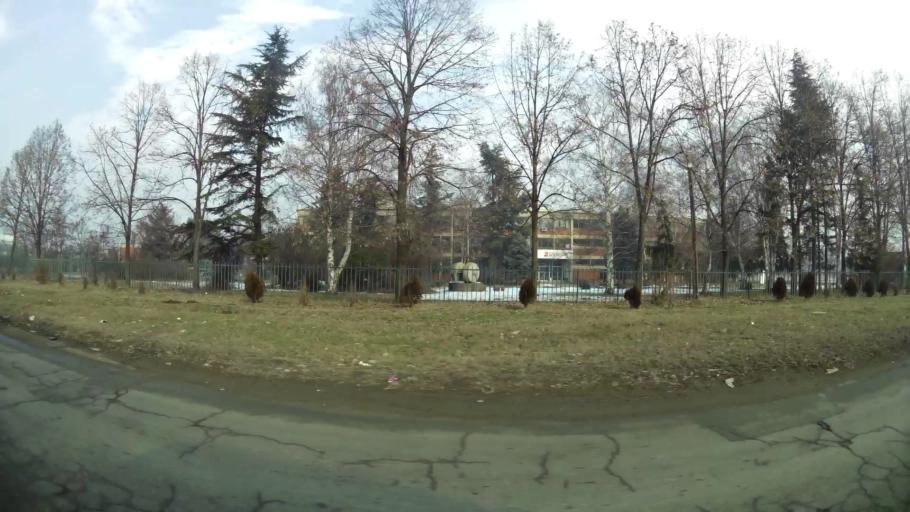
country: MK
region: Kisela Voda
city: Kisela Voda
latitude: 41.9923
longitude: 21.4922
